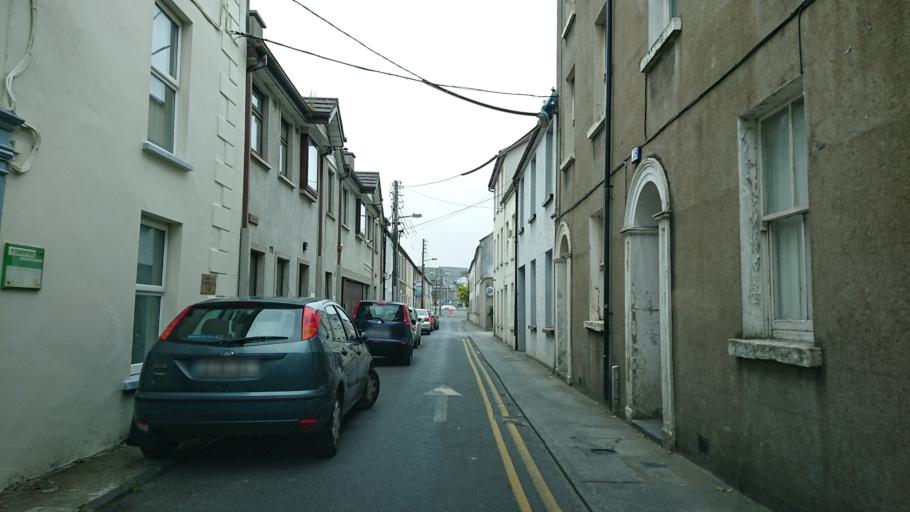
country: IE
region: Munster
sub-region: Waterford
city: Waterford
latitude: 52.2585
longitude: -7.1073
